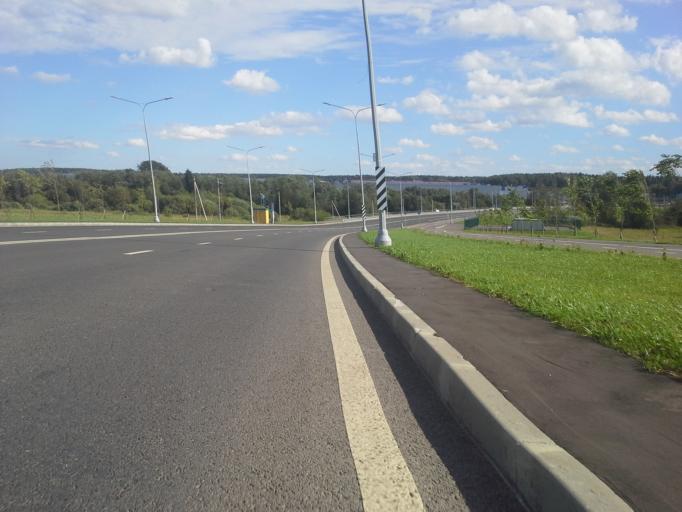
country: RU
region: Moskovskaya
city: Kokoshkino
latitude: 55.5862
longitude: 37.1620
